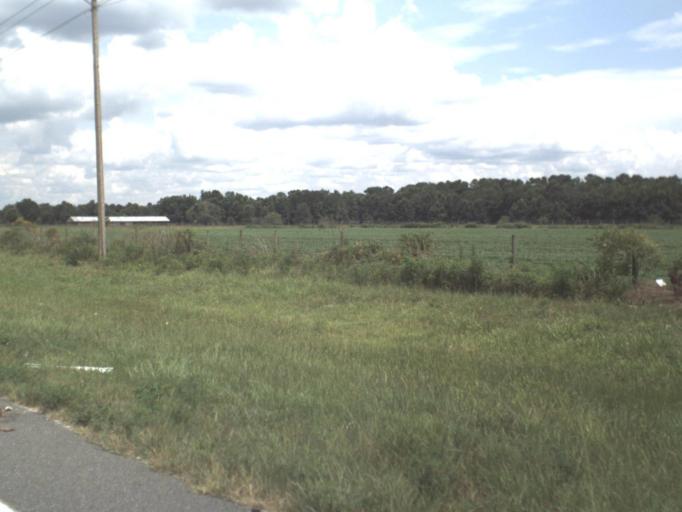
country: US
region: Florida
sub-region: Alachua County
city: Alachua
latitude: 29.8403
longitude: -82.3552
